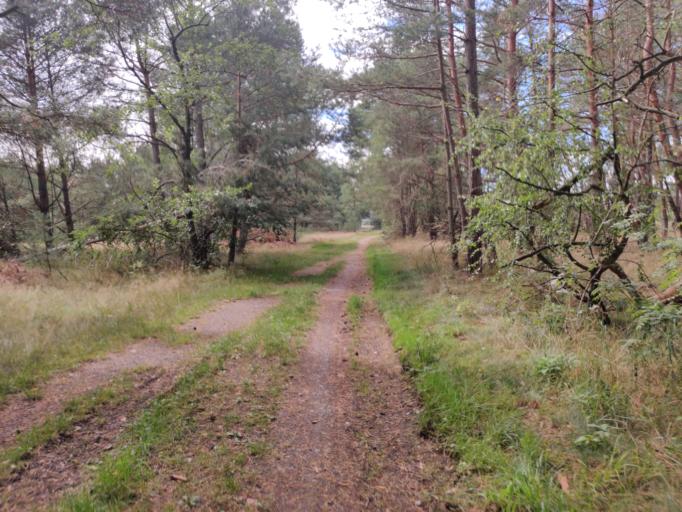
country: DE
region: Lower Saxony
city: Langelsheim
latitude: 51.9633
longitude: 10.3581
